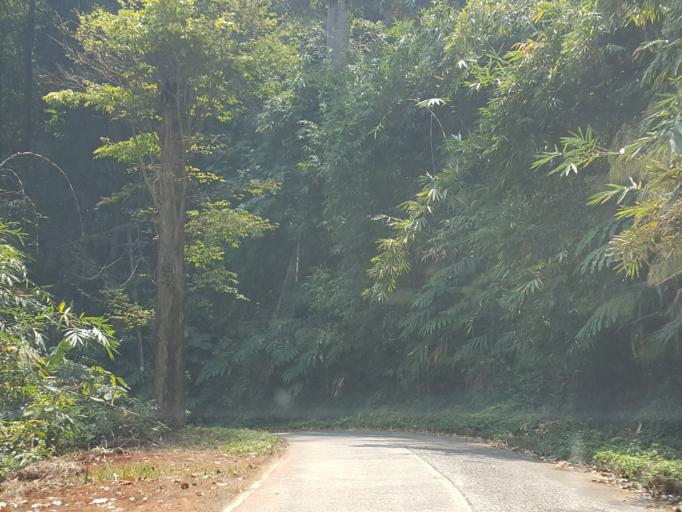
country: TH
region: Lampang
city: Mueang Pan
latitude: 18.8209
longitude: 99.4288
